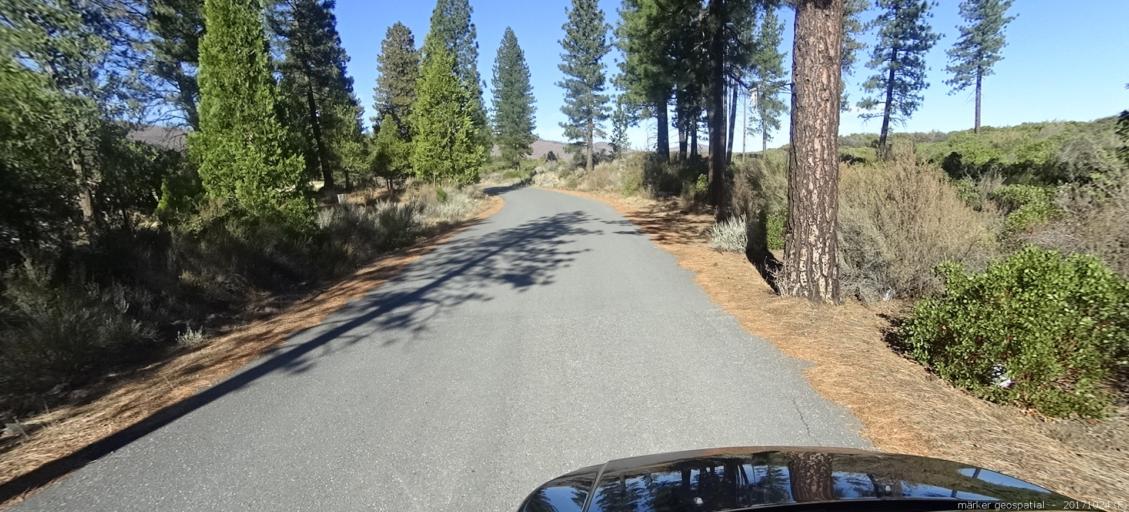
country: US
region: California
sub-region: Shasta County
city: Burney
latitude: 40.7492
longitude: -121.4708
